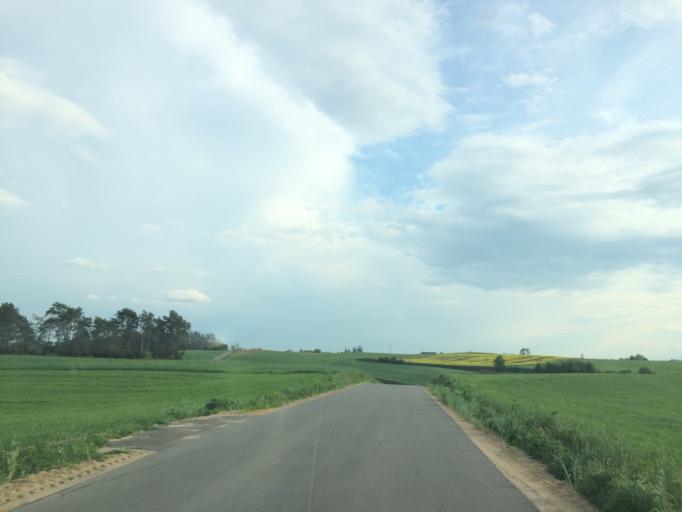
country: PL
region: Kujawsko-Pomorskie
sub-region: Powiat brodnicki
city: Brzozie
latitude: 53.3723
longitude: 19.7103
